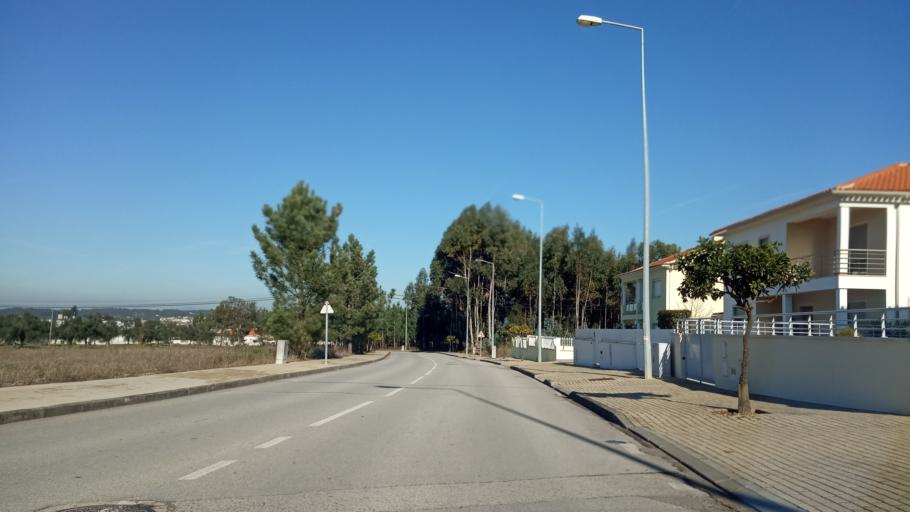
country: PT
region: Aveiro
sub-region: Anadia
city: Anadia
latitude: 40.4255
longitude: -8.4253
